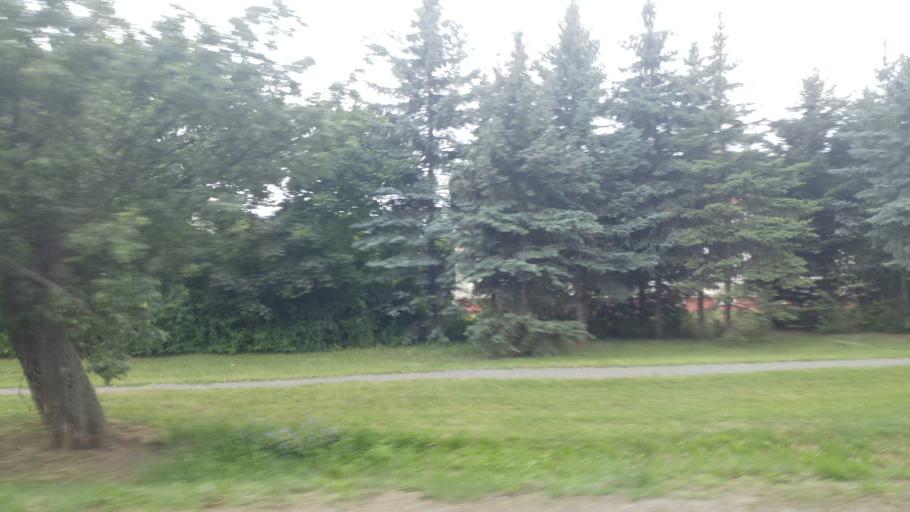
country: CZ
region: Central Bohemia
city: Roztoky
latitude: 50.1322
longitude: 14.3786
